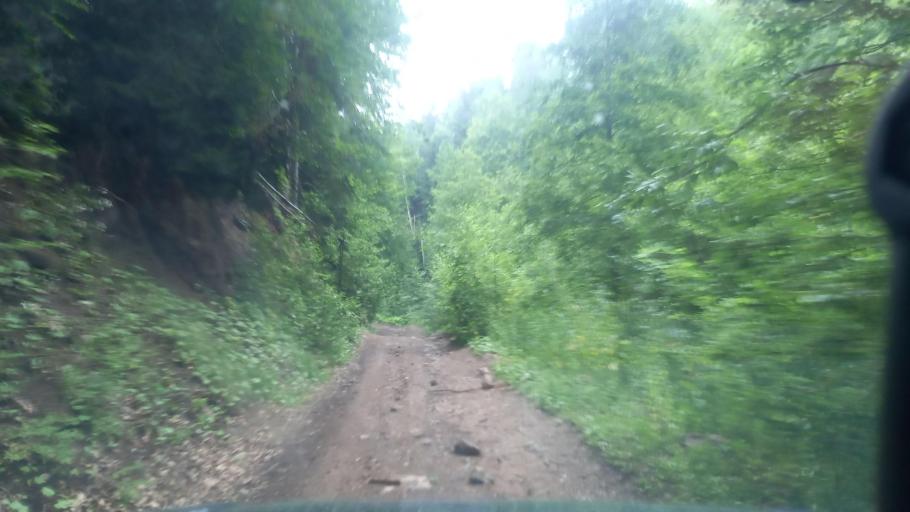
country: RU
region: Karachayevo-Cherkesiya
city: Kurdzhinovo
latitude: 43.8148
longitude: 40.8876
